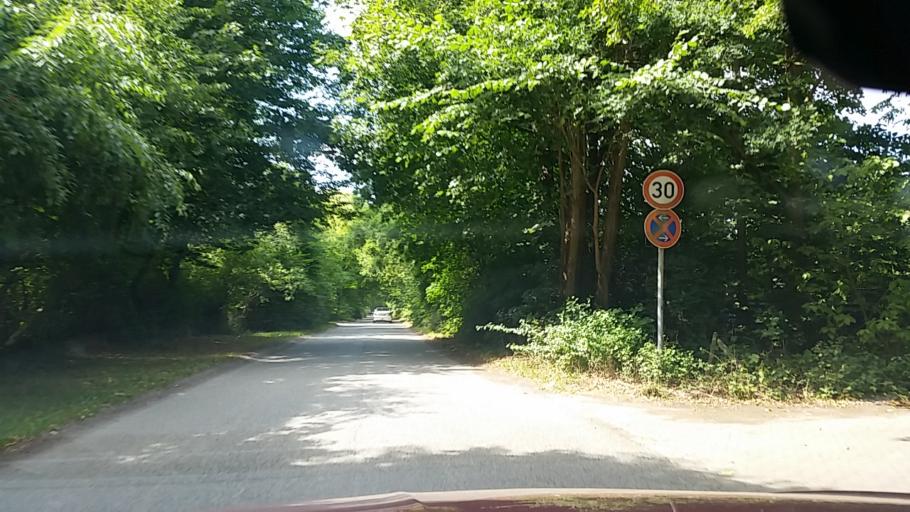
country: DE
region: Lower Saxony
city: Hannover
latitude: 52.3405
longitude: 9.7520
